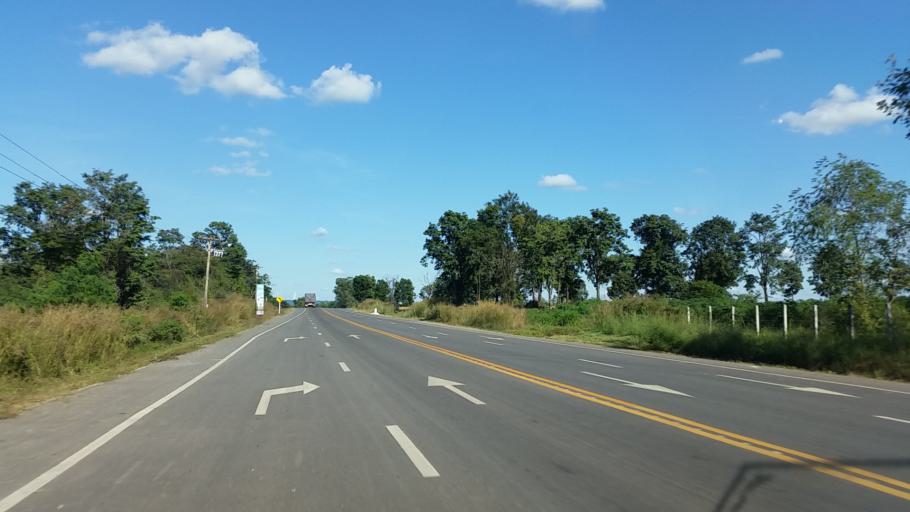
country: TH
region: Chaiyaphum
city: Thep Sathit
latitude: 15.5402
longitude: 101.4343
